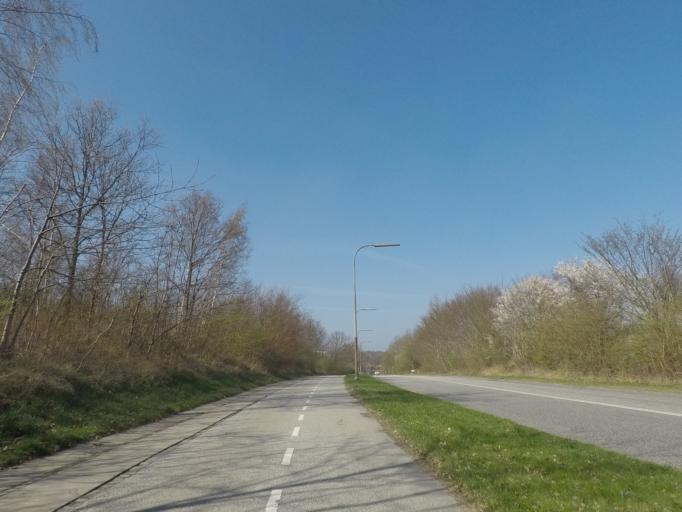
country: DK
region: Capital Region
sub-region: Ballerup Kommune
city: Ballerup
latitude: 55.7460
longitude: 12.3842
